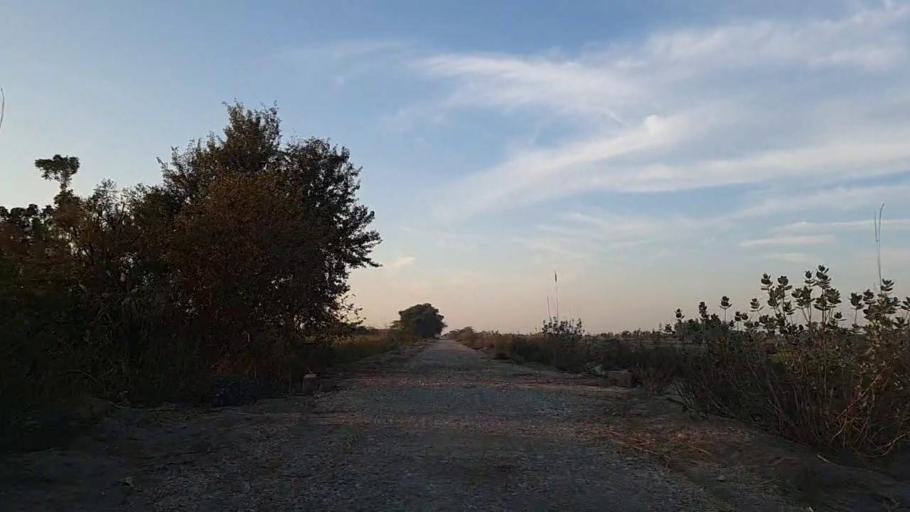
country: PK
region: Sindh
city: Bandhi
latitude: 26.6155
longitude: 68.3547
